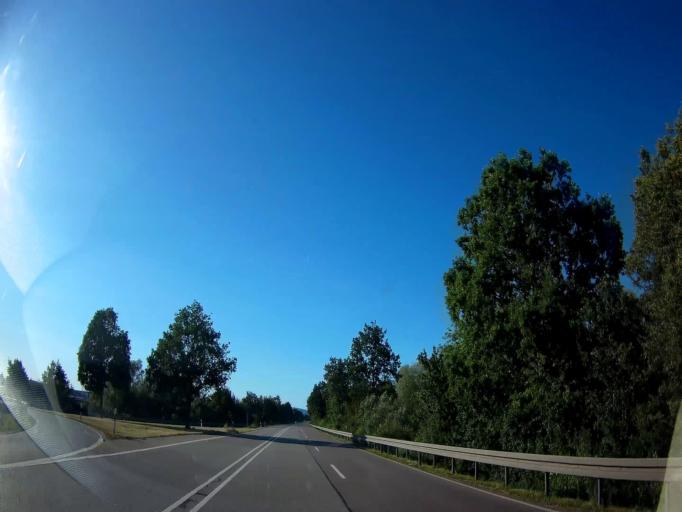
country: DE
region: Bavaria
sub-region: Lower Bavaria
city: Parkstetten
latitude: 48.8862
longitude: 12.6187
